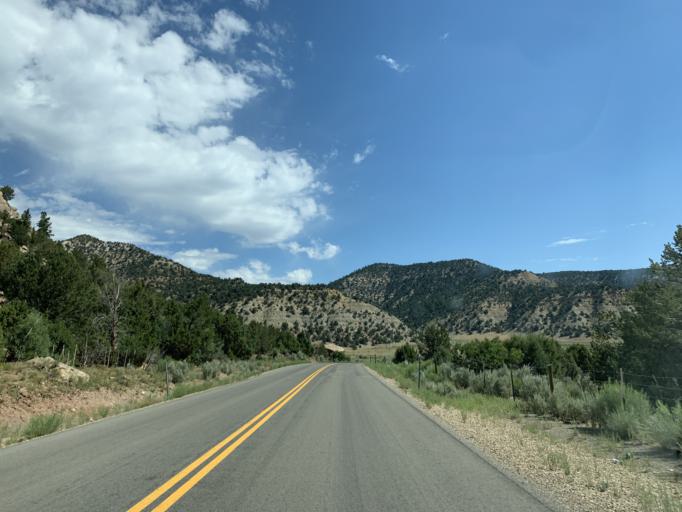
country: US
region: Utah
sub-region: Carbon County
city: East Carbon City
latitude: 39.7718
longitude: -110.5162
